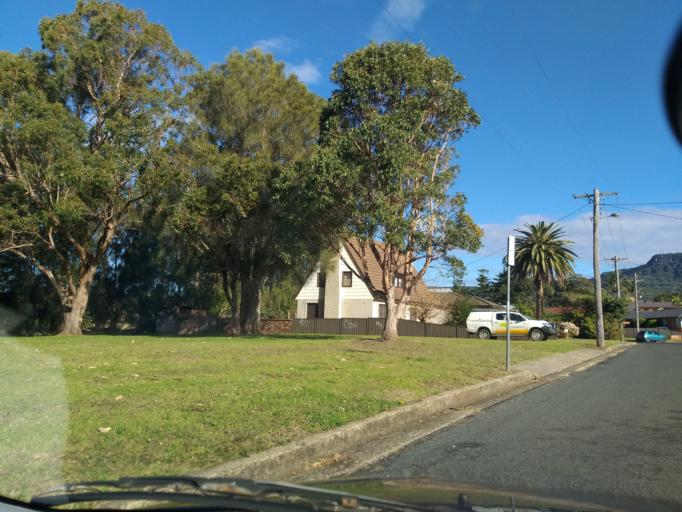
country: AU
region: New South Wales
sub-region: Wollongong
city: East Corrimal
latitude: -34.3720
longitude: 150.9115
